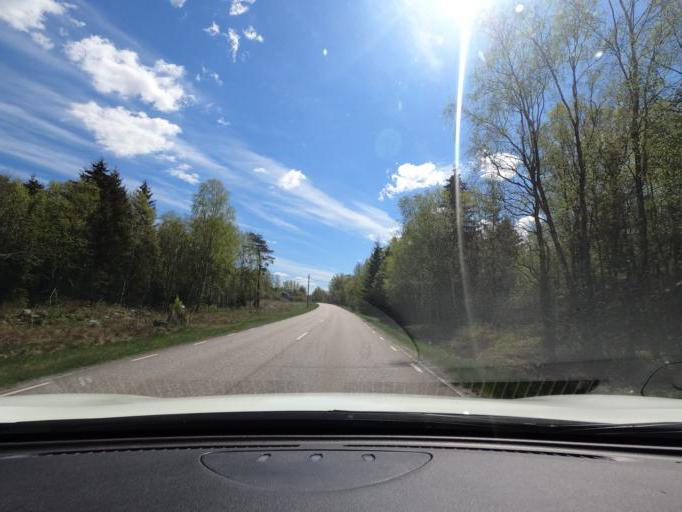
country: SE
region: Halland
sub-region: Kungsbacka Kommun
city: Fjaeras kyrkby
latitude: 57.3984
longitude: 12.2361
